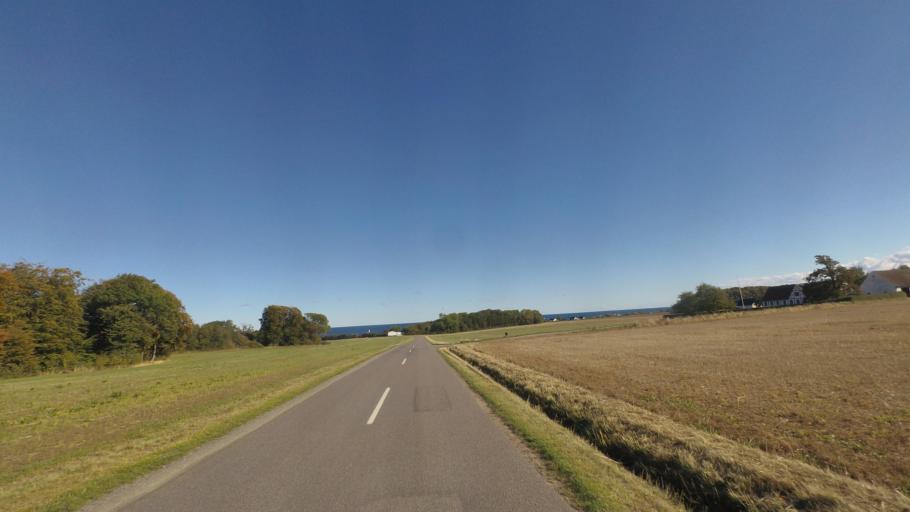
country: DK
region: Capital Region
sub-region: Bornholm Kommune
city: Nexo
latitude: 55.1107
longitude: 15.1304
